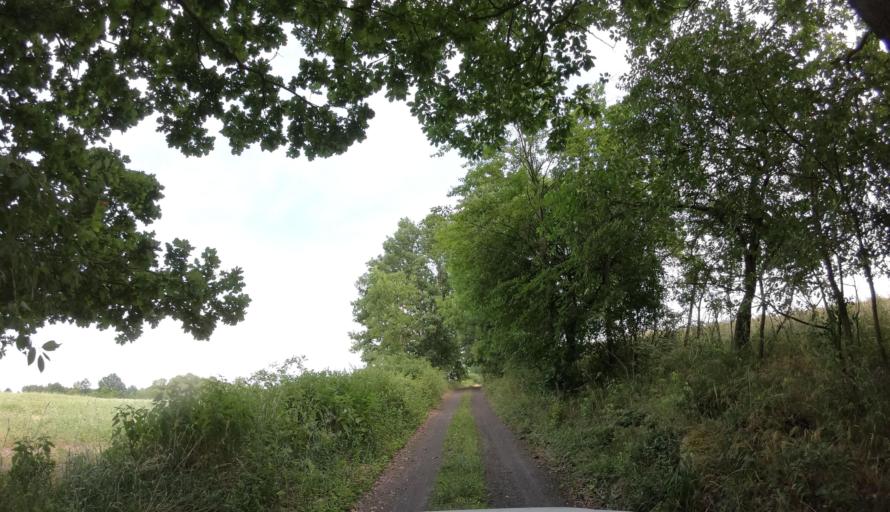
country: PL
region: West Pomeranian Voivodeship
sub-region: Powiat pyrzycki
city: Kozielice
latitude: 53.0298
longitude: 14.7543
